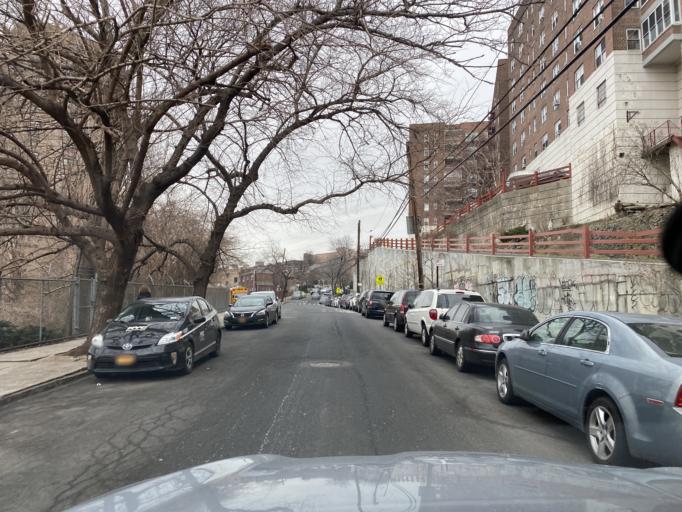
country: US
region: New York
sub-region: New York County
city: Inwood
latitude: 40.8692
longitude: -73.9068
